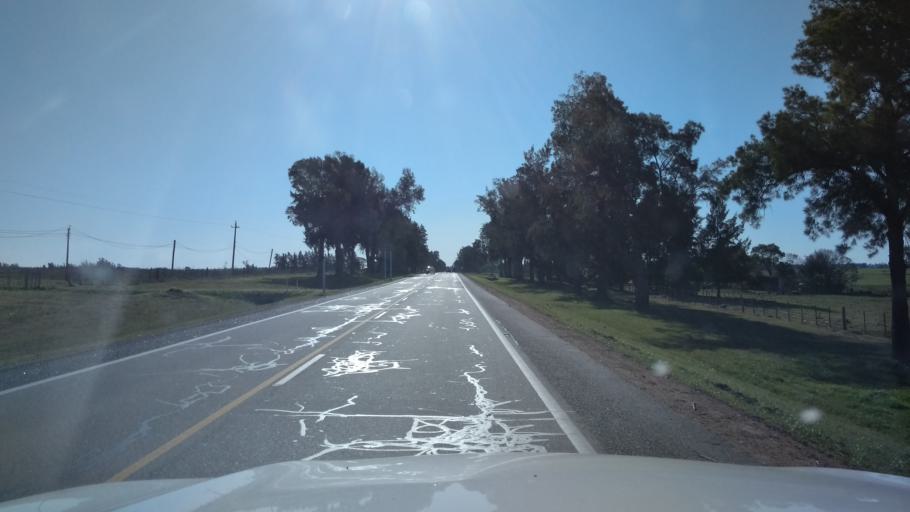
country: UY
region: Canelones
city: San Jacinto
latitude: -34.5874
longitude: -55.8386
